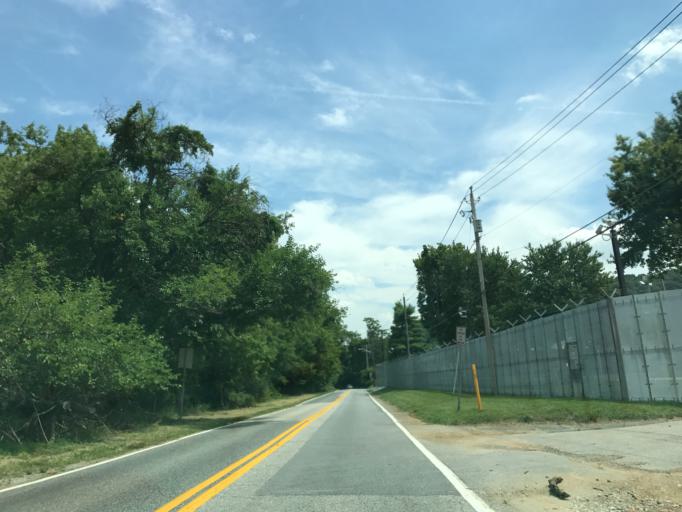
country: US
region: Maryland
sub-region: Baltimore County
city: Cockeysville
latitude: 39.4943
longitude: -76.6810
